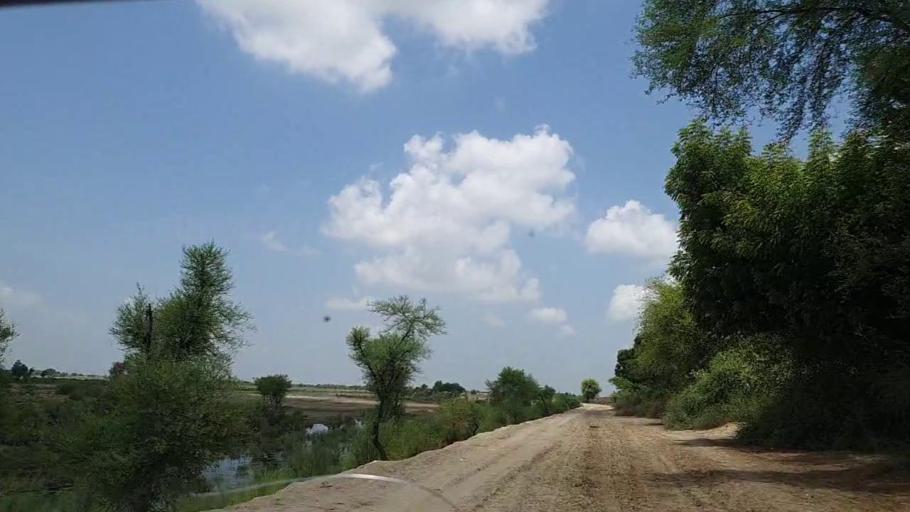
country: PK
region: Sindh
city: Tharu Shah
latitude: 26.9632
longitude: 68.0302
